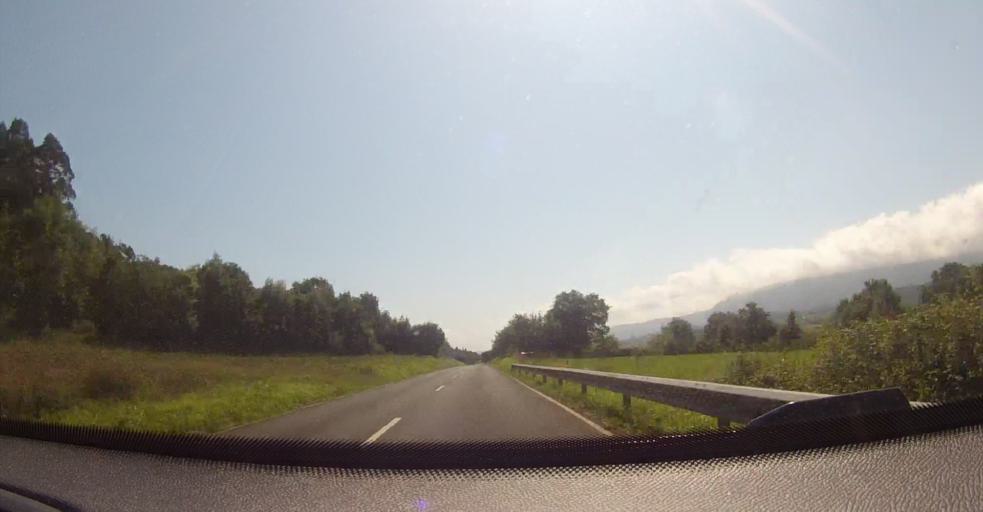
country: ES
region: Asturias
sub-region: Province of Asturias
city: Colunga
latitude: 43.4891
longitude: -5.3064
